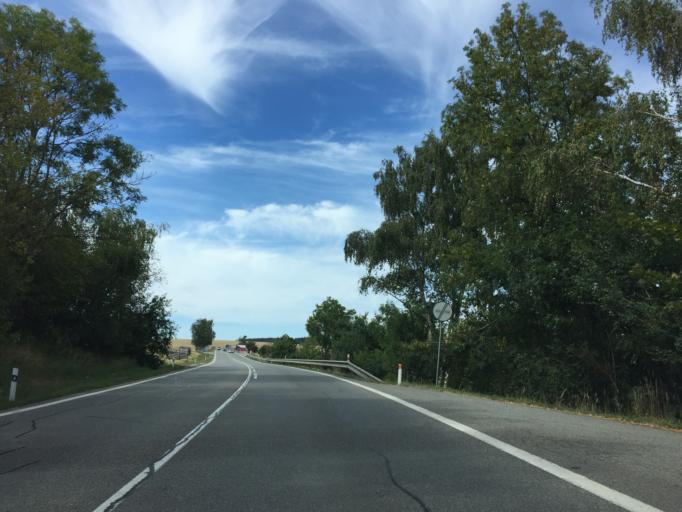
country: CZ
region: Jihocesky
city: Chotoviny
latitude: 49.5554
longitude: 14.6660
